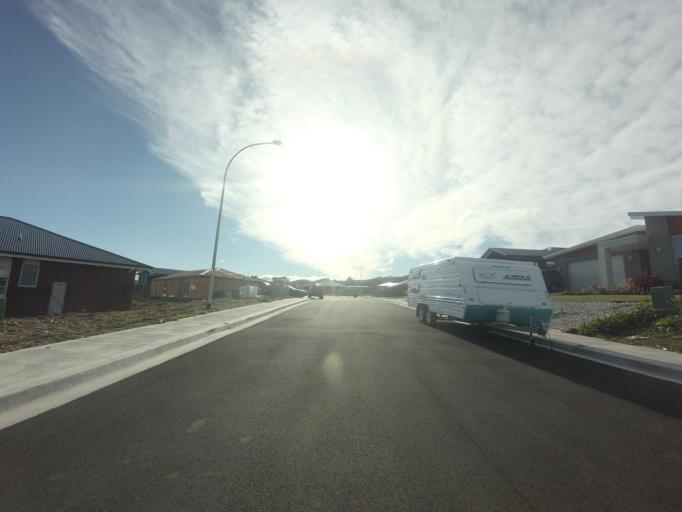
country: AU
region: Tasmania
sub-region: Clarence
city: Rokeby
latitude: -42.9034
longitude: 147.4537
